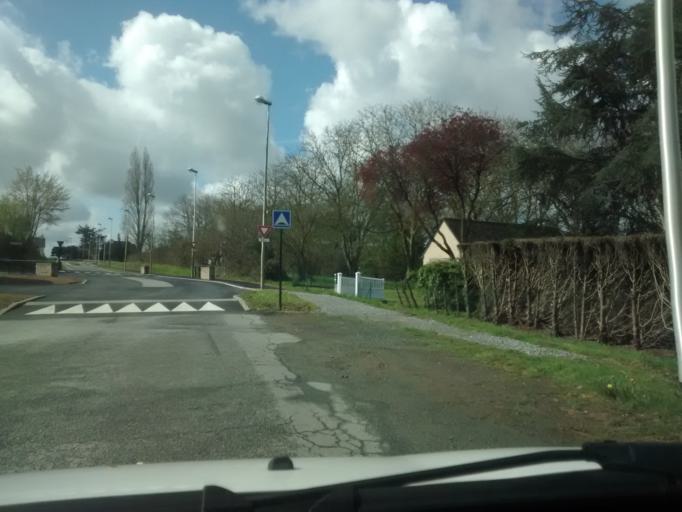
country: FR
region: Brittany
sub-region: Departement d'Ille-et-Vilaine
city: Acigne
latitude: 48.1416
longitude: -1.5315
